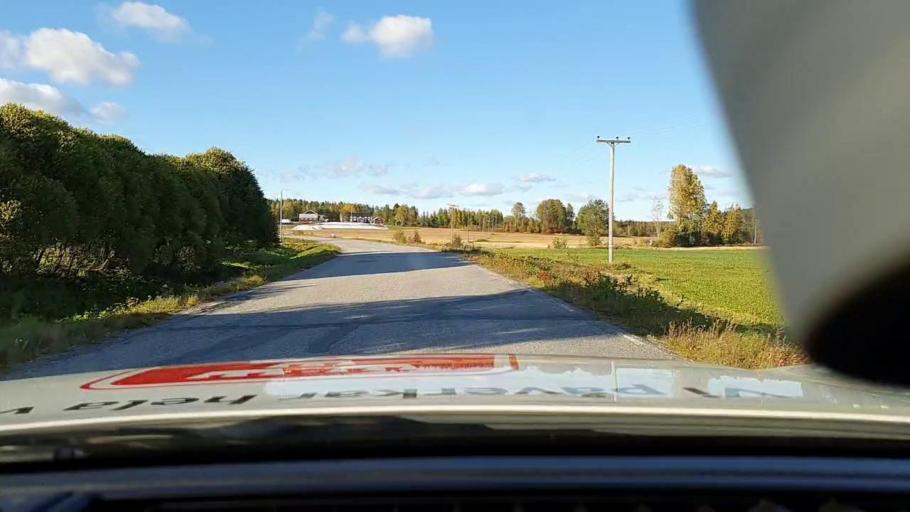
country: SE
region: Norrbotten
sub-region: Pitea Kommun
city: Norrfjarden
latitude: 65.5230
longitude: 21.4920
